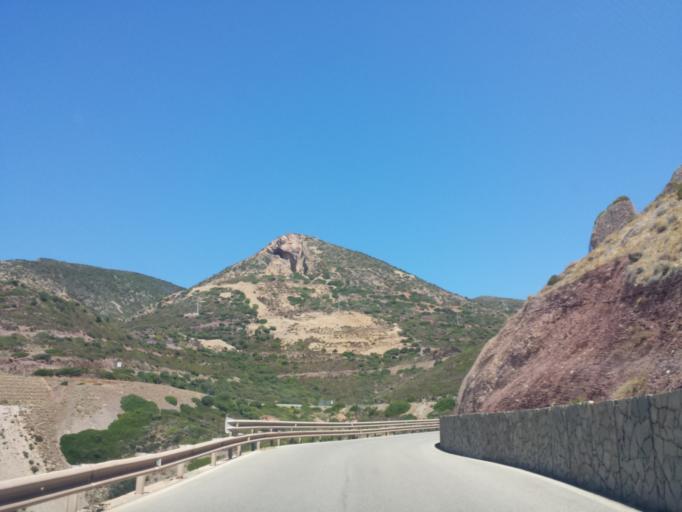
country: IT
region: Sardinia
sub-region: Provincia di Carbonia-Iglesias
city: Gonnesa
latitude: 39.3067
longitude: 8.4367
